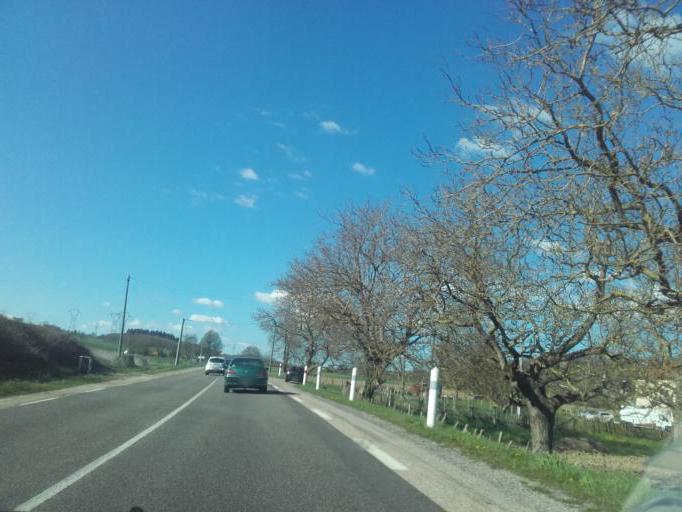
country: FR
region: Rhone-Alpes
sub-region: Departement de l'Isere
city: Champier
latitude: 45.4642
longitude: 5.2933
